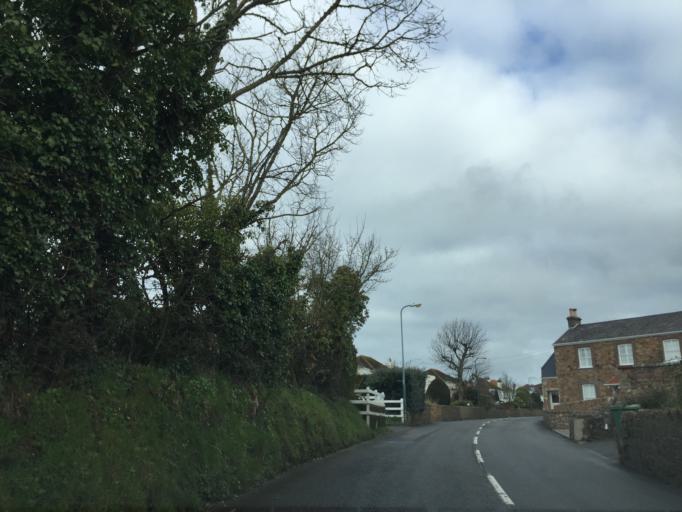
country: JE
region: St Helier
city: Saint Helier
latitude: 49.2048
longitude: -2.1416
